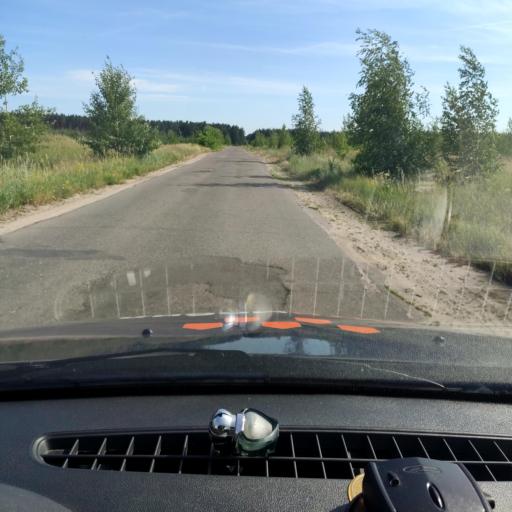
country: RU
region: Voronezj
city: Somovo
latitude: 51.7828
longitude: 39.3736
